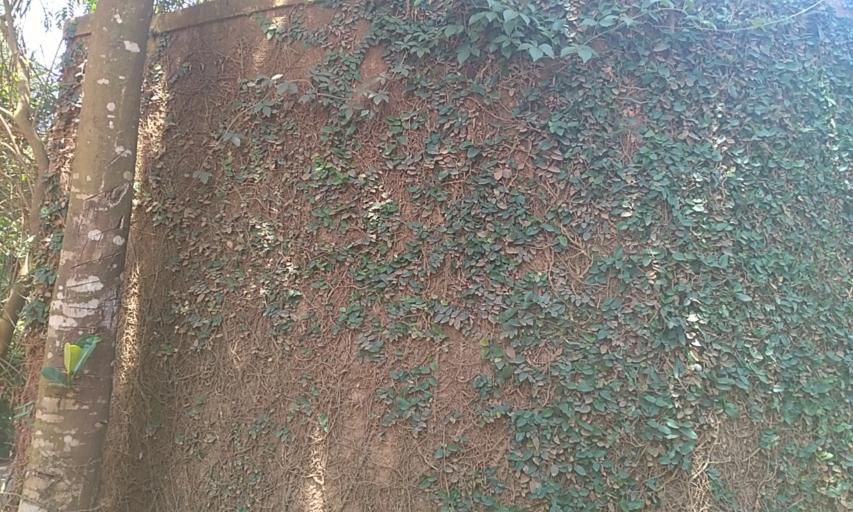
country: UG
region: Central Region
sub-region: Wakiso District
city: Wakiso
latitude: 0.4123
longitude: 32.4750
